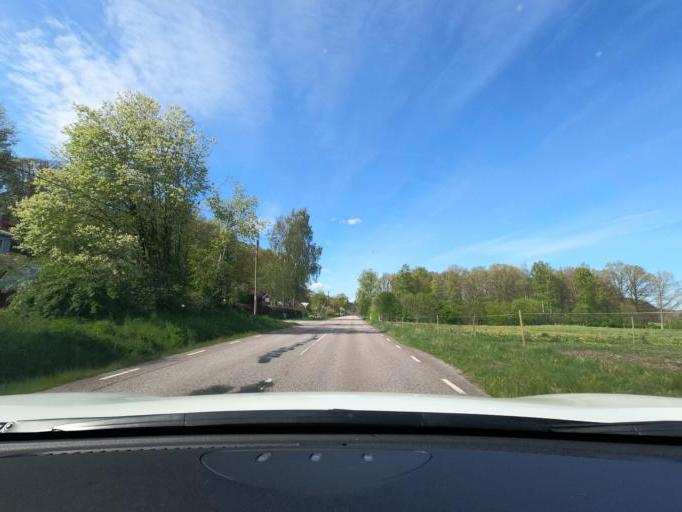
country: SE
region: Vaestra Goetaland
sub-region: Marks Kommun
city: Kinna
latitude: 57.4706
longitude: 12.5935
